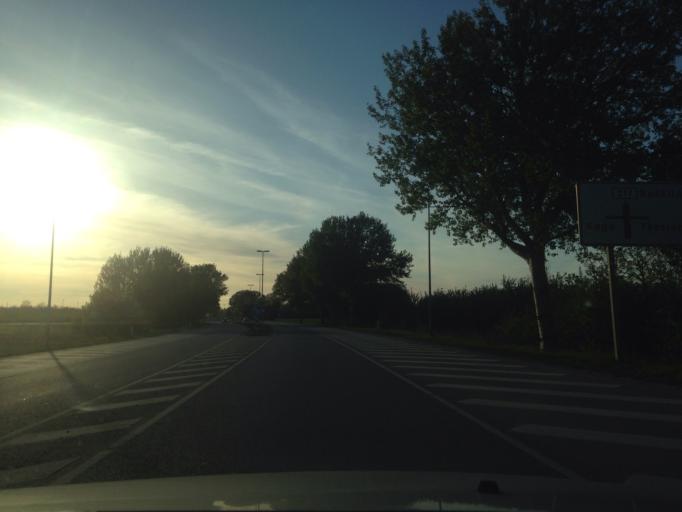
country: DK
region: Zealand
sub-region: Greve Kommune
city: Greve
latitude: 55.5882
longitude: 12.2504
